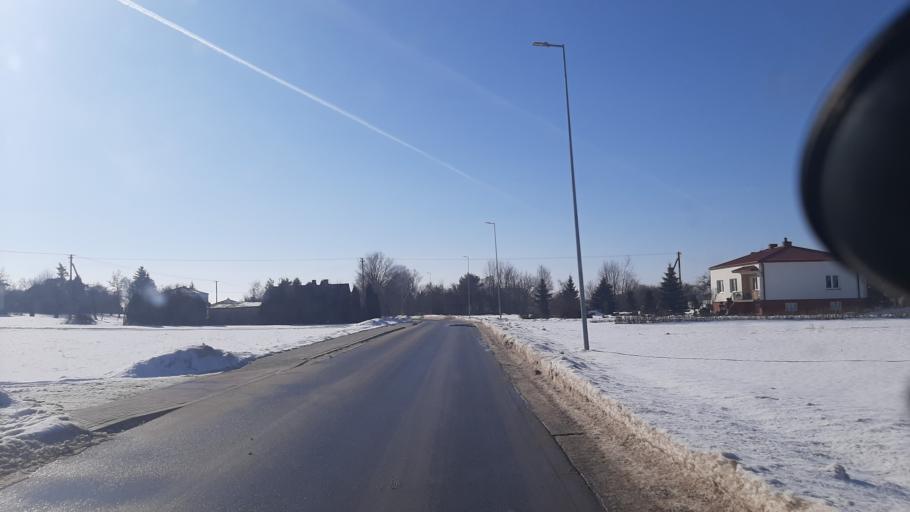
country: PL
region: Lublin Voivodeship
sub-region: Powiat lubelski
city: Garbow
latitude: 51.3037
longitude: 22.3075
